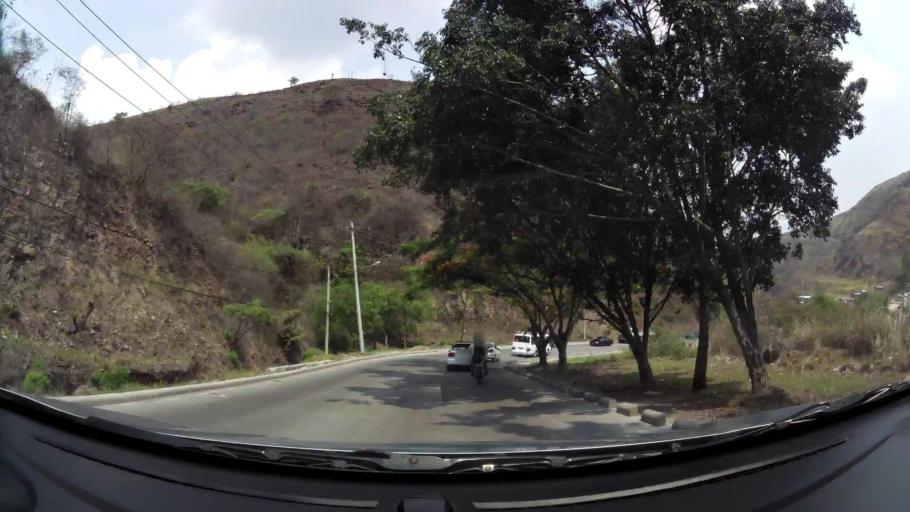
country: HN
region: Francisco Morazan
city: Tegucigalpa
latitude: 14.1188
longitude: -87.2183
